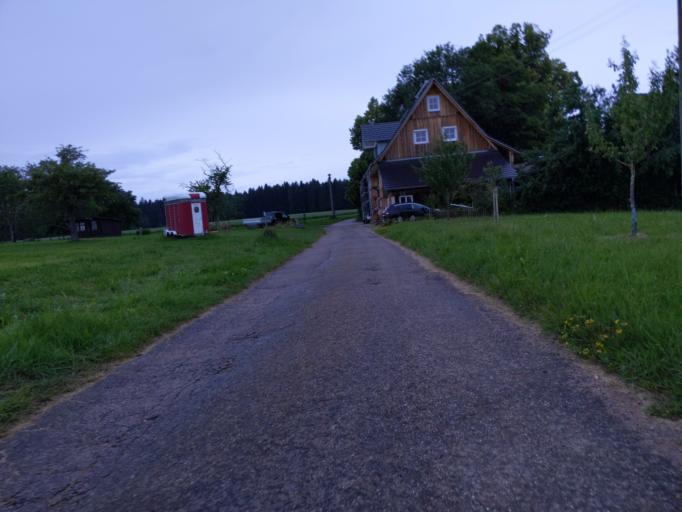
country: DE
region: Baden-Wuerttemberg
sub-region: Karlsruhe Region
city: Alpirsbach
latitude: 48.3385
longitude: 8.4293
